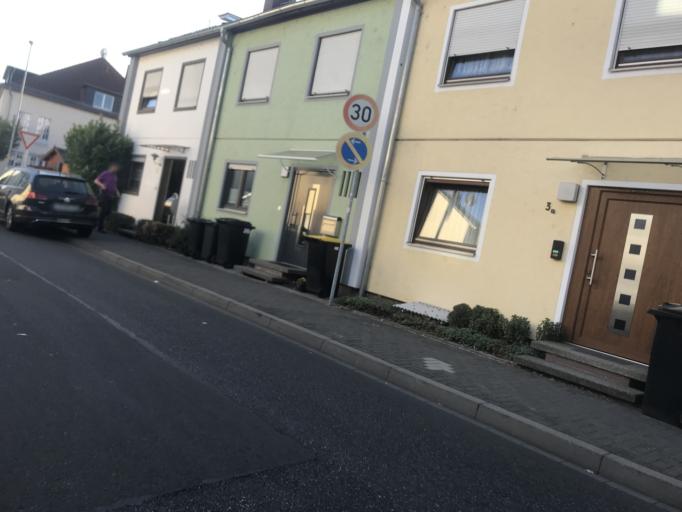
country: DE
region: Rheinland-Pfalz
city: Mainz
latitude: 50.0013
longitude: 8.3018
